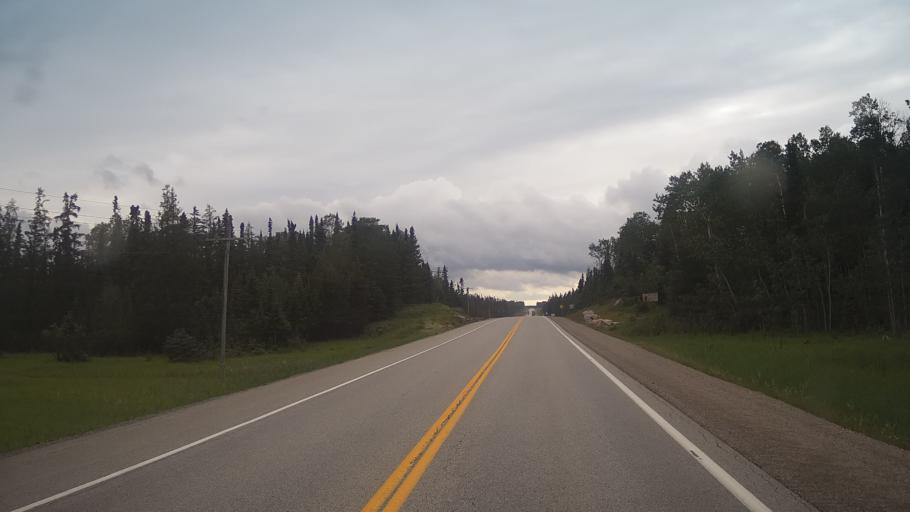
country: CA
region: Ontario
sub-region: Thunder Bay District
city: Thunder Bay
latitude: 48.9412
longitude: -90.1631
